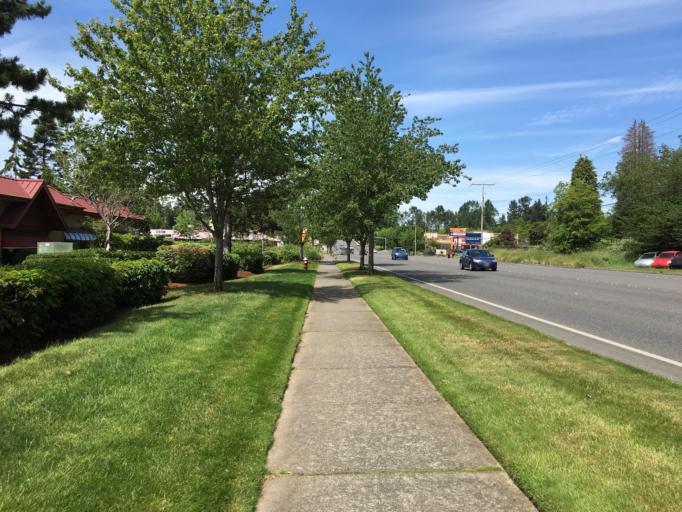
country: US
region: Washington
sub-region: Whatcom County
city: Bellingham
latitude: 48.7984
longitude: -122.4862
